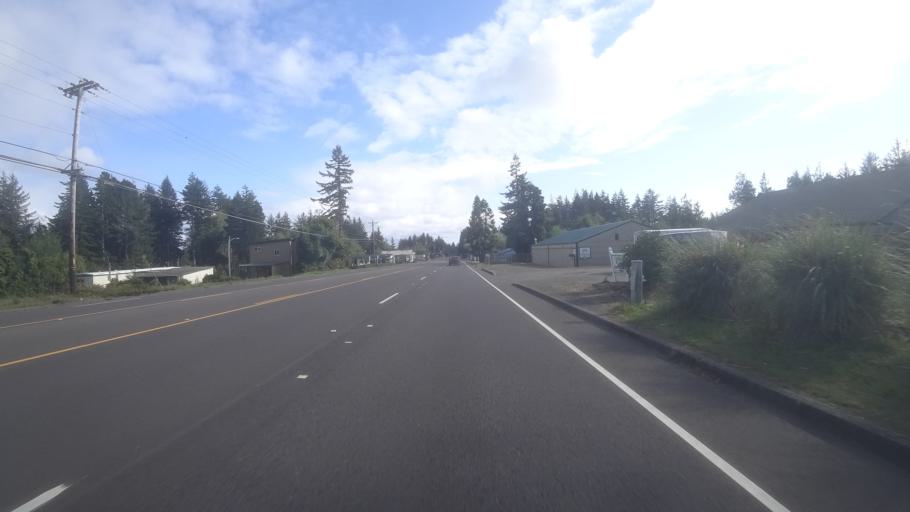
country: US
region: Oregon
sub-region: Lane County
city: Florence
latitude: 43.9489
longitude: -124.1043
